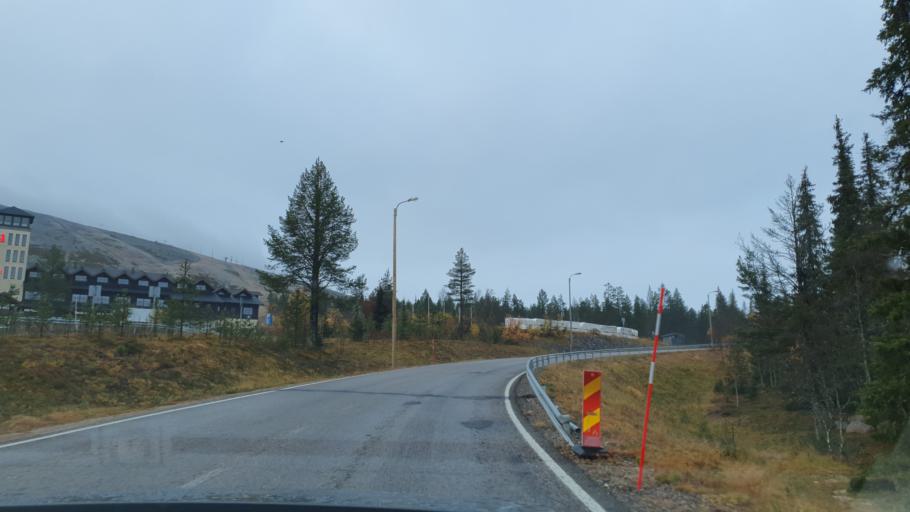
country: FI
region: Lapland
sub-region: Tunturi-Lappi
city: Kolari
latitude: 67.5818
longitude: 24.2016
